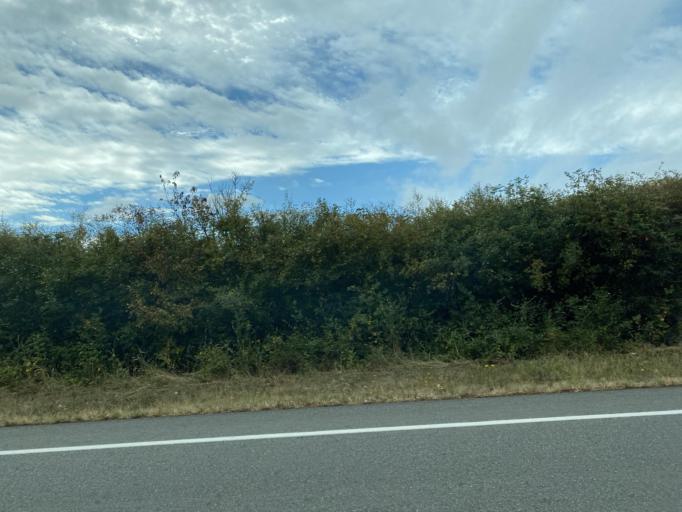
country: US
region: Washington
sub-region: Island County
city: Coupeville
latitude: 48.2171
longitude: -122.7002
